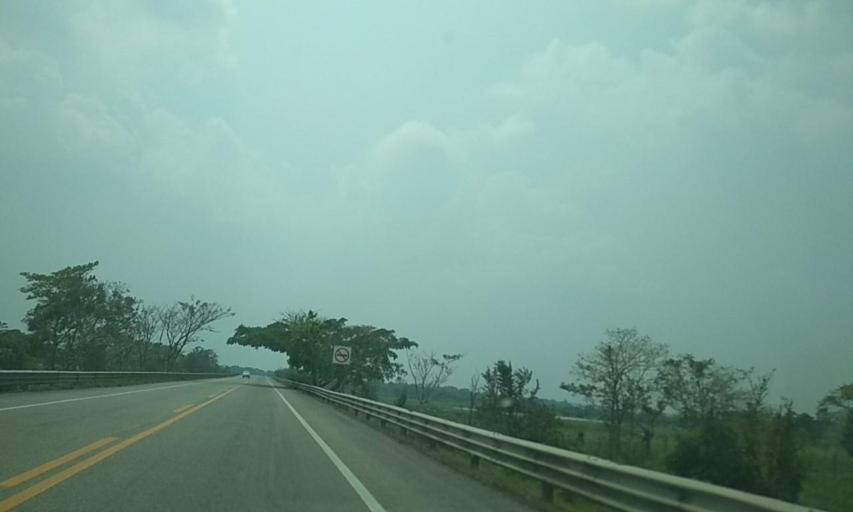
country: MX
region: Tabasco
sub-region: Huimanguillo
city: Francisco Rueda
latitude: 17.7680
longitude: -94.0322
